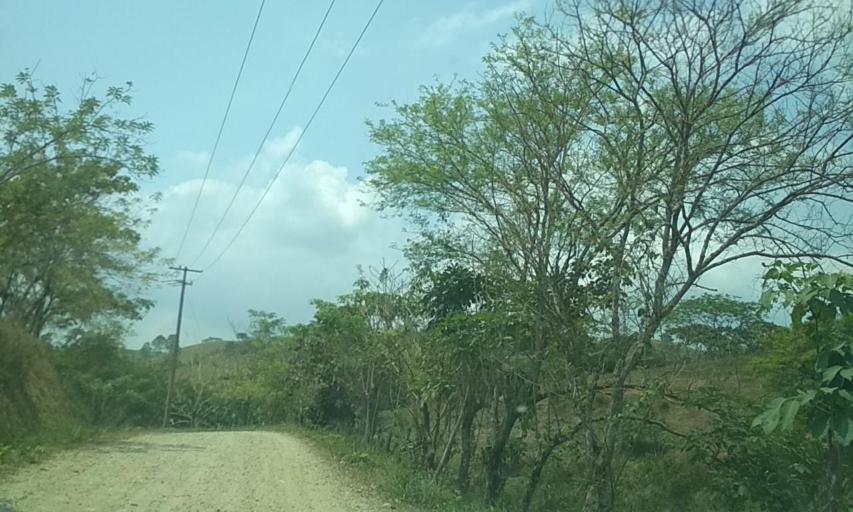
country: MX
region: Tabasco
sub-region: Huimanguillo
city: Francisco Rueda
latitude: 17.6294
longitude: -93.8213
